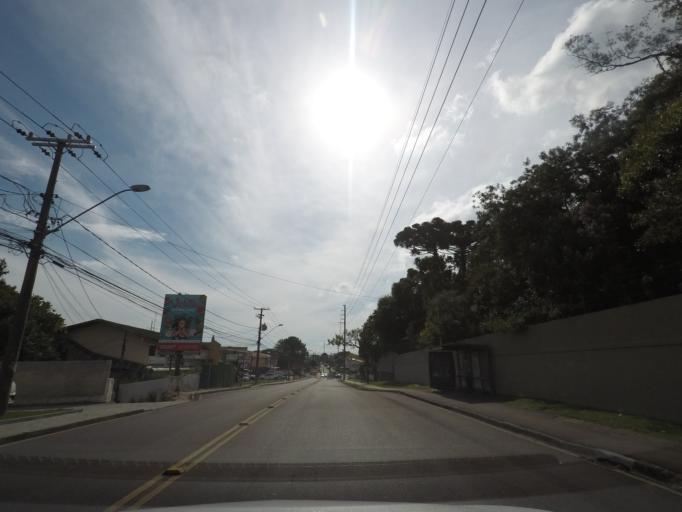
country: BR
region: Parana
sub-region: Pinhais
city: Pinhais
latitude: -25.4711
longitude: -49.2386
